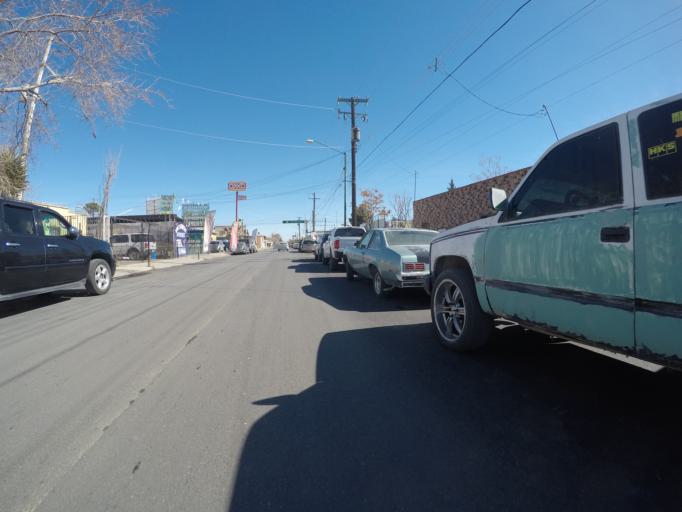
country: MX
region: Chihuahua
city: Ciudad Juarez
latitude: 31.7405
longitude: -106.4648
